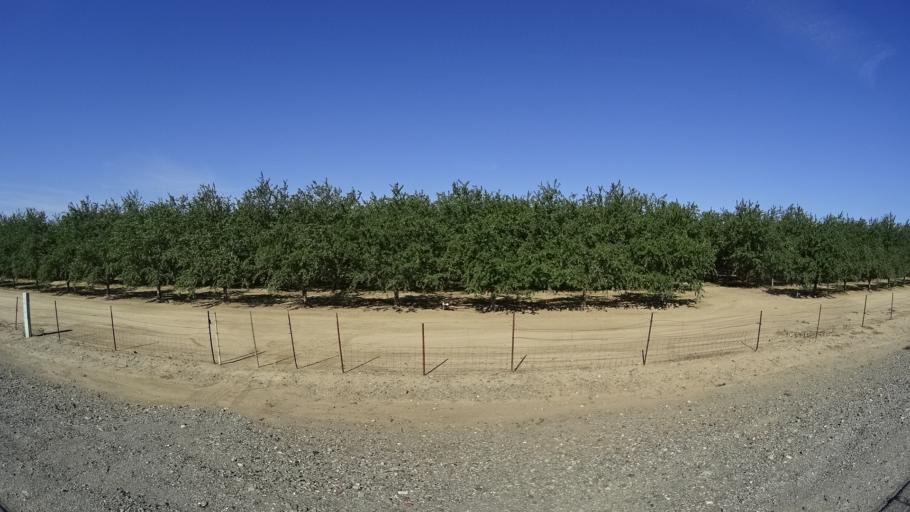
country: US
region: California
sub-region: Glenn County
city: Orland
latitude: 39.6751
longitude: -122.1970
